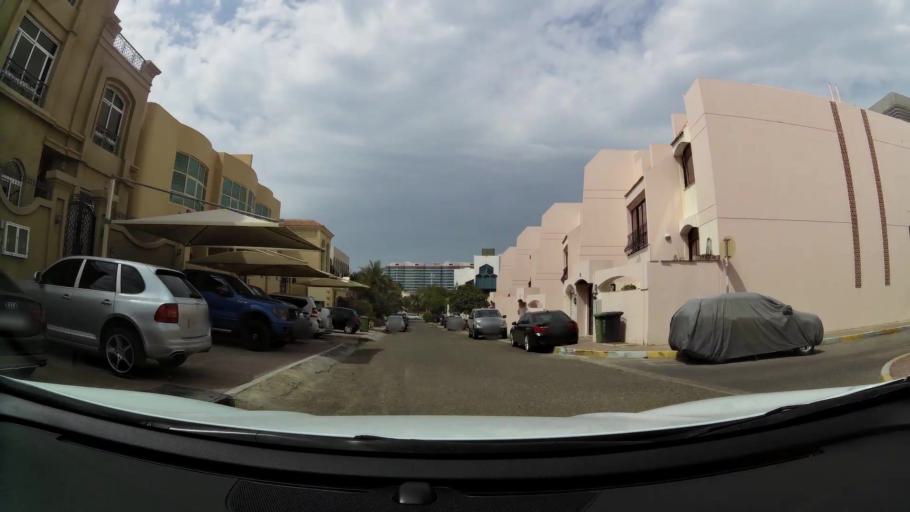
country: AE
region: Abu Dhabi
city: Abu Dhabi
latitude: 24.4641
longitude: 54.3390
